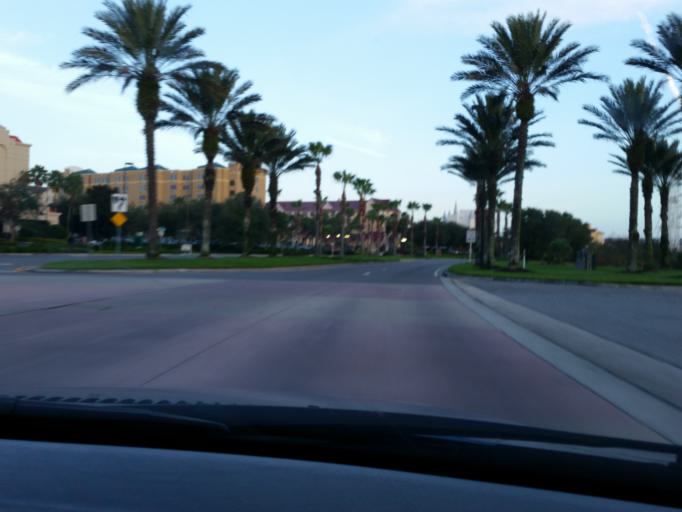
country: US
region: Florida
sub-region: Orange County
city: Doctor Phillips
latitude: 28.4357
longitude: -81.4672
